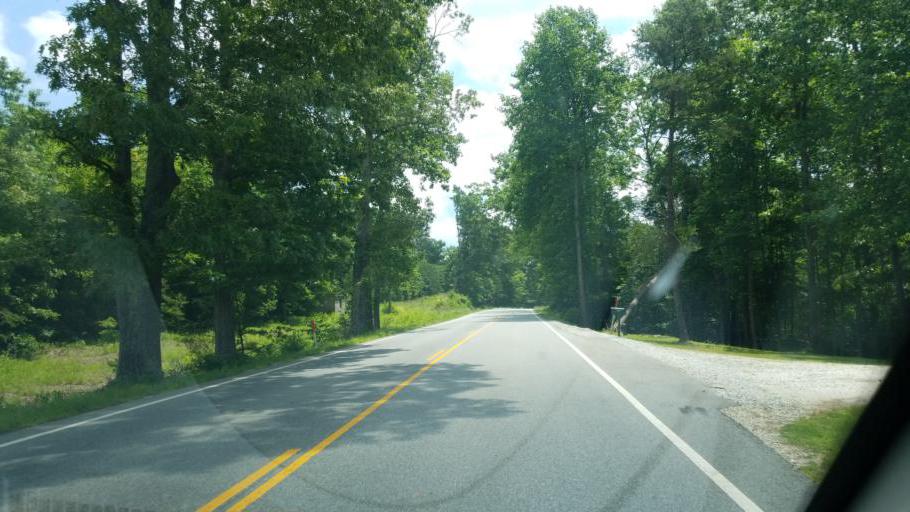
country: US
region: Virginia
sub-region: Nelson County
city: Lovingston
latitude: 37.5672
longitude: -78.8495
